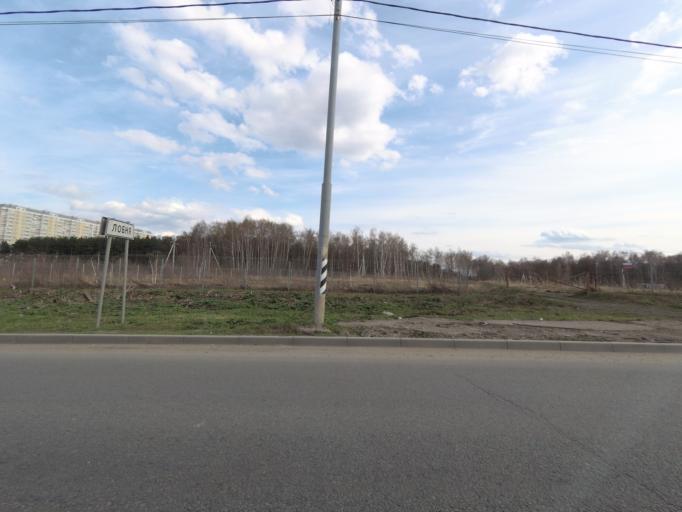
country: RU
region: Moskovskaya
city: Lobnya
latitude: 56.0058
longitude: 37.4332
